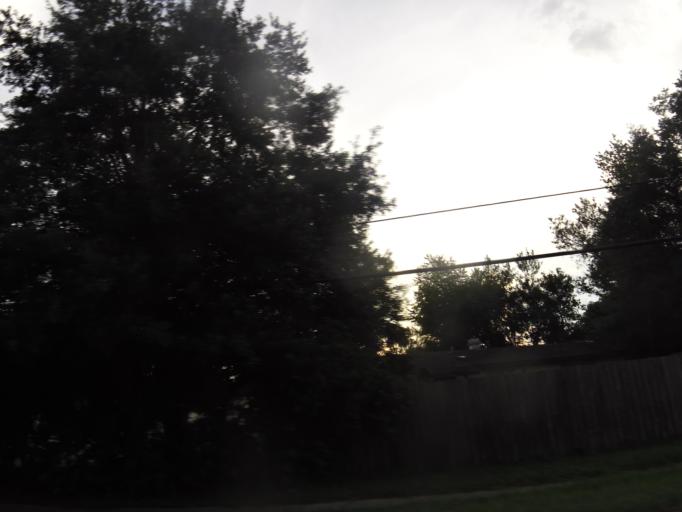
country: US
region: Florida
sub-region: Clay County
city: Bellair-Meadowbrook Terrace
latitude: 30.2883
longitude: -81.7813
